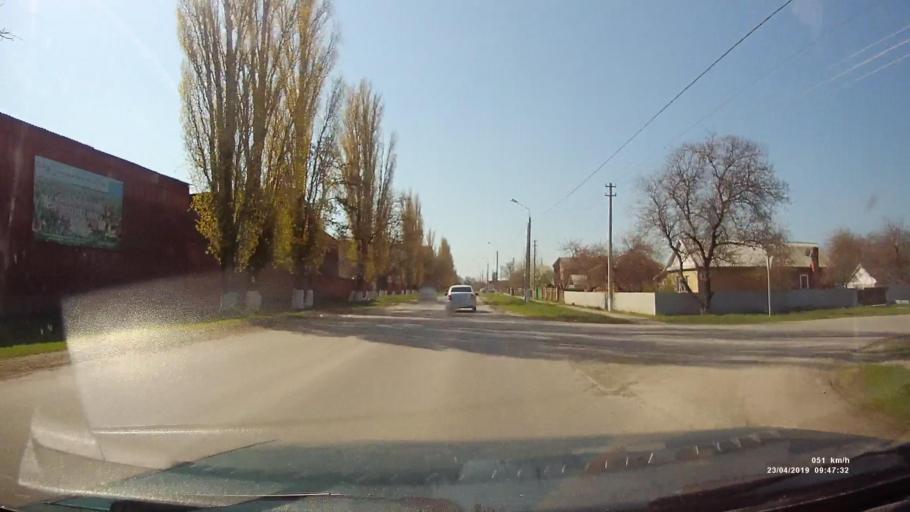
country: RU
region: Rostov
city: Orlovskiy
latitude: 46.8747
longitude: 42.0384
